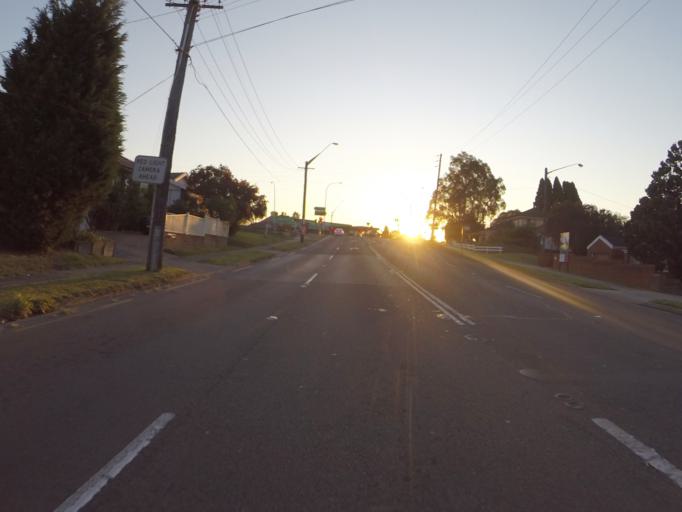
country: AU
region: New South Wales
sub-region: Hurstville
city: Penshurst
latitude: -33.9579
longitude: 151.0705
